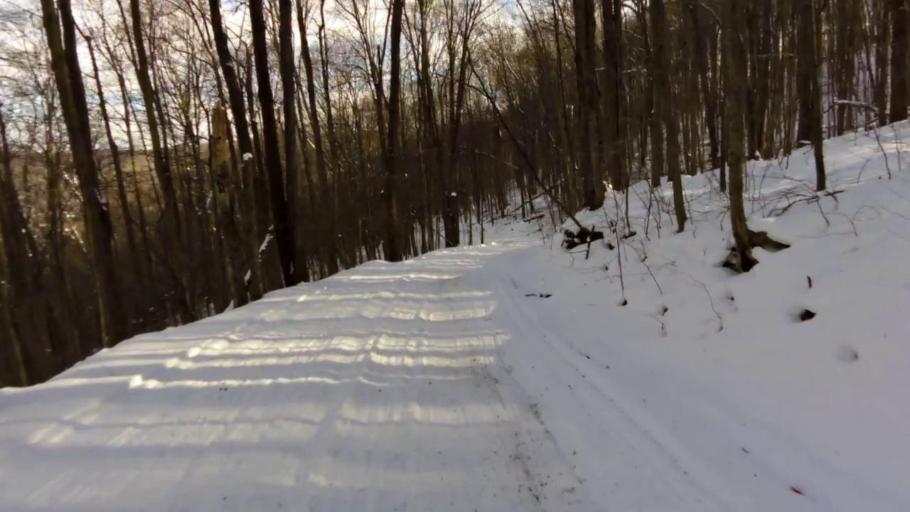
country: US
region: Pennsylvania
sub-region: McKean County
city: Foster Brook
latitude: 42.0641
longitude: -78.6527
